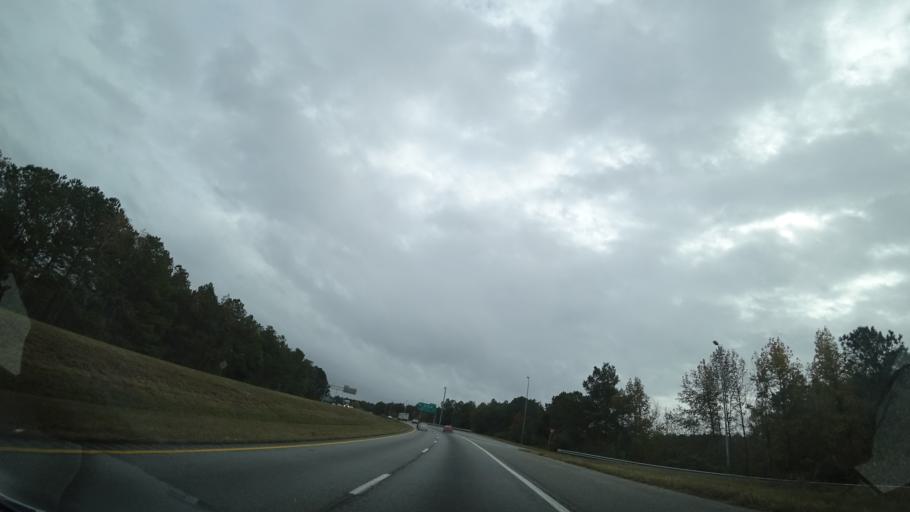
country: US
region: Virginia
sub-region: City of Portsmouth
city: Portsmouth Heights
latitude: 36.7883
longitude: -76.4253
